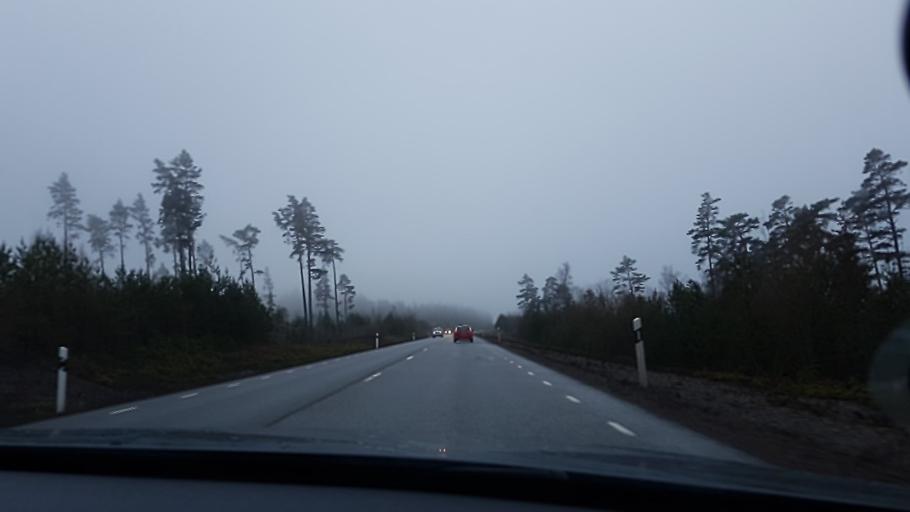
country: SE
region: Vaestra Goetaland
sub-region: Gullspangs Kommun
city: Gullspang
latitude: 58.8812
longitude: 14.0118
